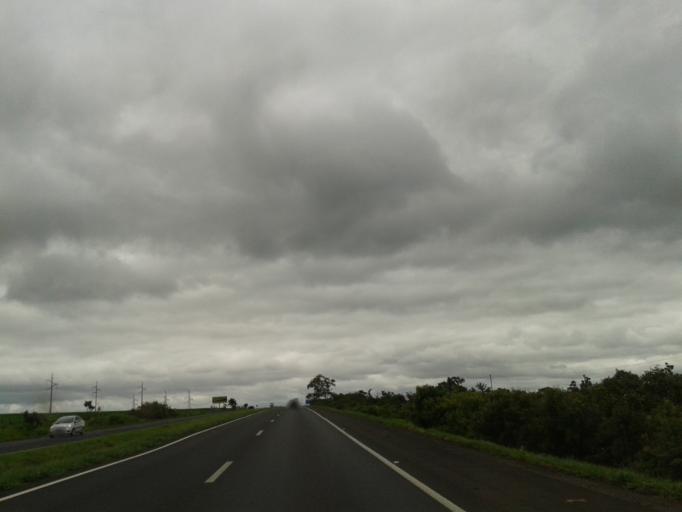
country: BR
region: Minas Gerais
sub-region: Uberlandia
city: Uberlandia
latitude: -19.0280
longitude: -48.2030
